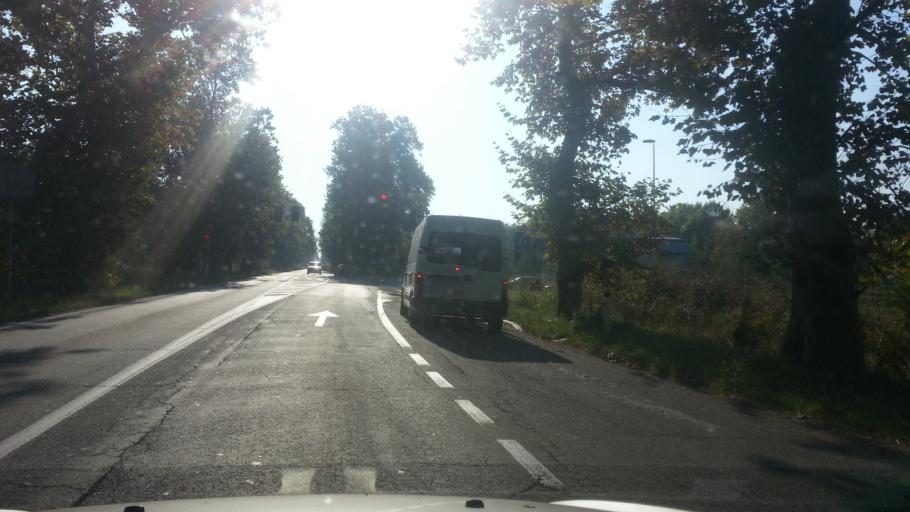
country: RS
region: Central Serbia
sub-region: Belgrade
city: Zemun
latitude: 44.8753
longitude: 20.3406
